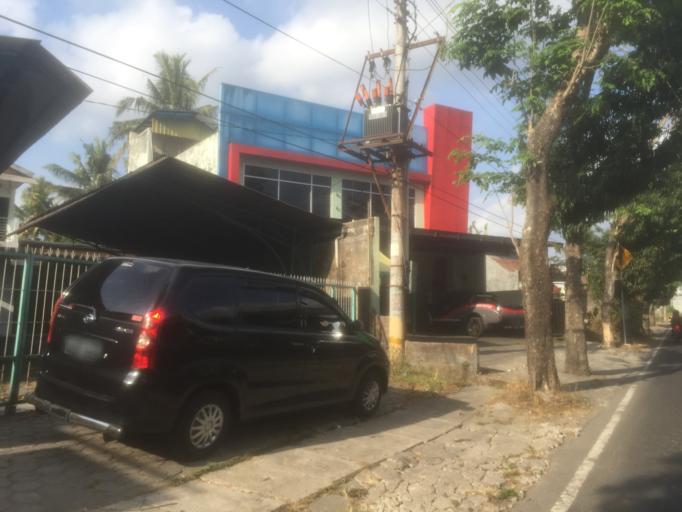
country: ID
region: Daerah Istimewa Yogyakarta
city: Melati
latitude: -7.7189
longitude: 110.3724
